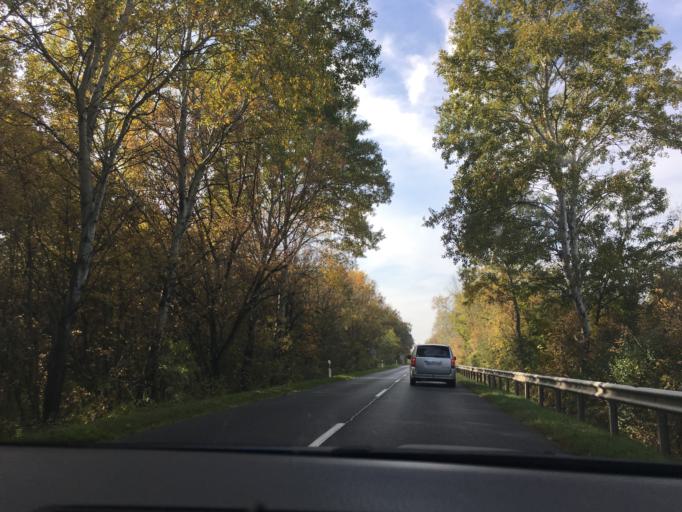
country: HU
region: Hajdu-Bihar
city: Vamospercs
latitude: 47.5279
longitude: 21.8519
